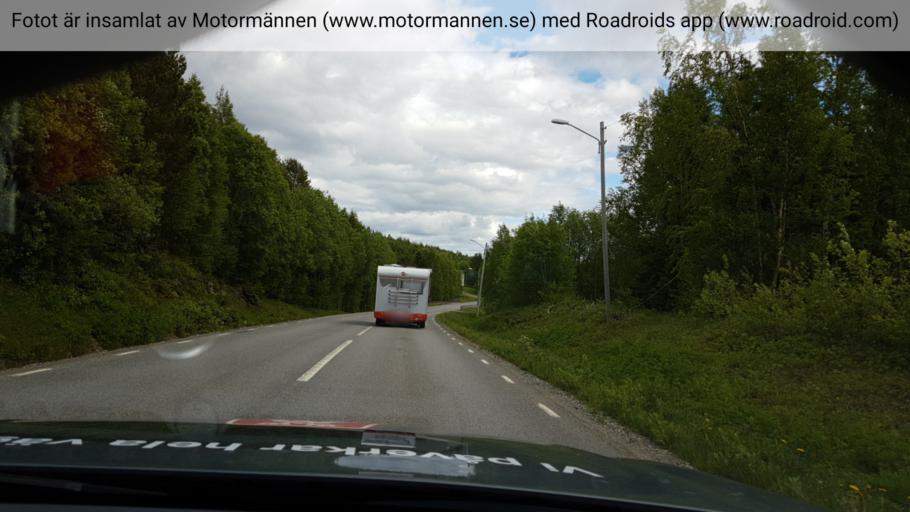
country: NO
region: Nord-Trondelag
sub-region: Lierne
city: Sandvika
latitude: 64.3889
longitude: 14.5246
